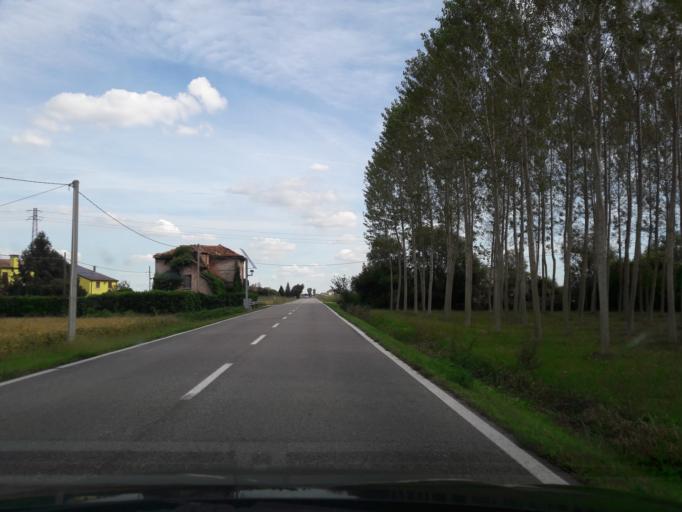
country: IT
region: Veneto
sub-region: Provincia di Padova
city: Piacenza d'Adige
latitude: 45.0915
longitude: 11.5360
